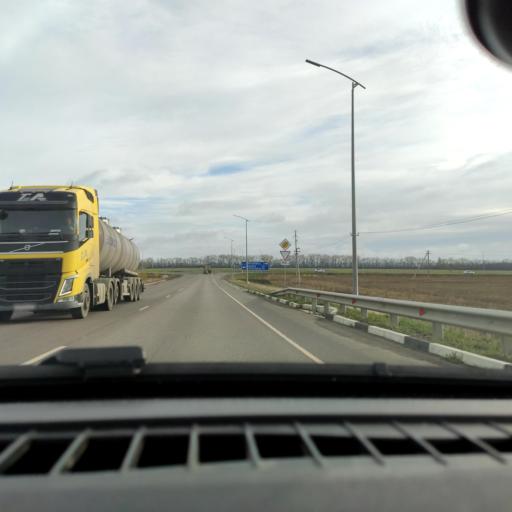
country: RU
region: Belgorod
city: Ilovka
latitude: 50.6864
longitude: 38.6577
